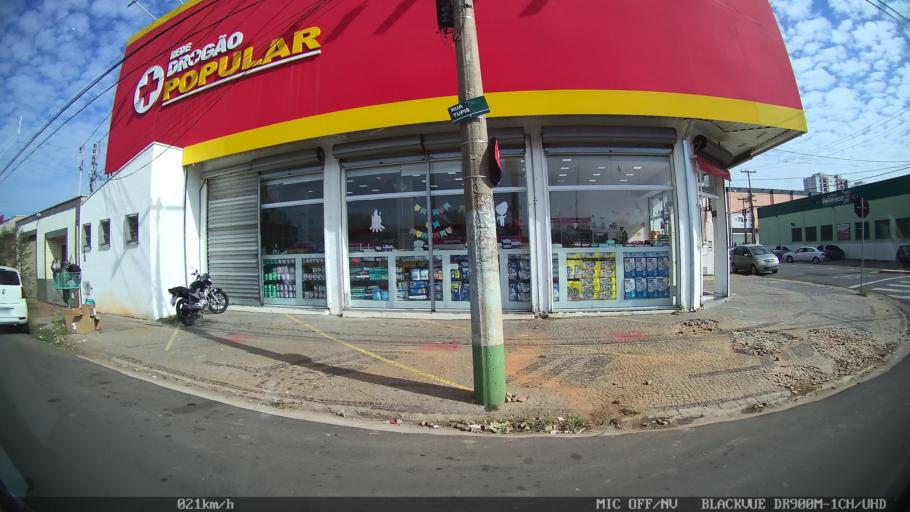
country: BR
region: Sao Paulo
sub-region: Santa Barbara D'Oeste
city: Santa Barbara d'Oeste
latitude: -22.7611
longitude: -47.3961
